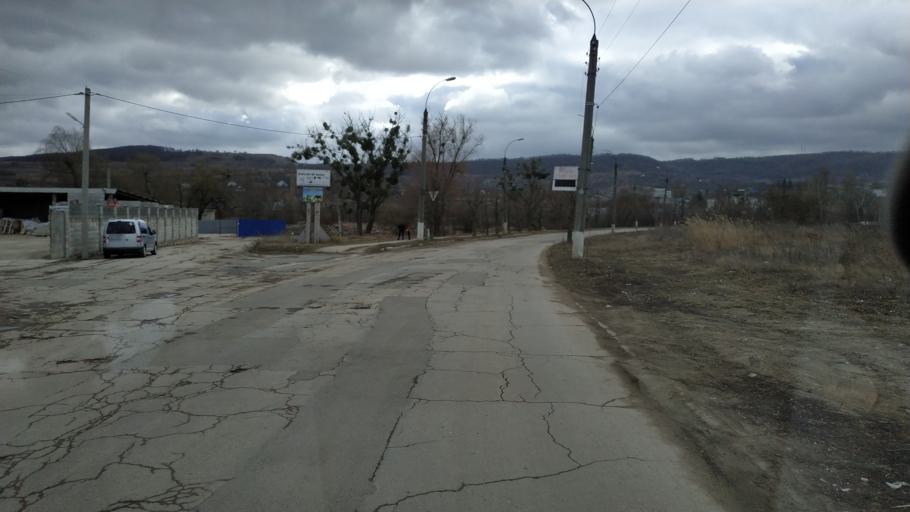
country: MD
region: Calarasi
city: Calarasi
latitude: 47.2464
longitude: 28.3167
